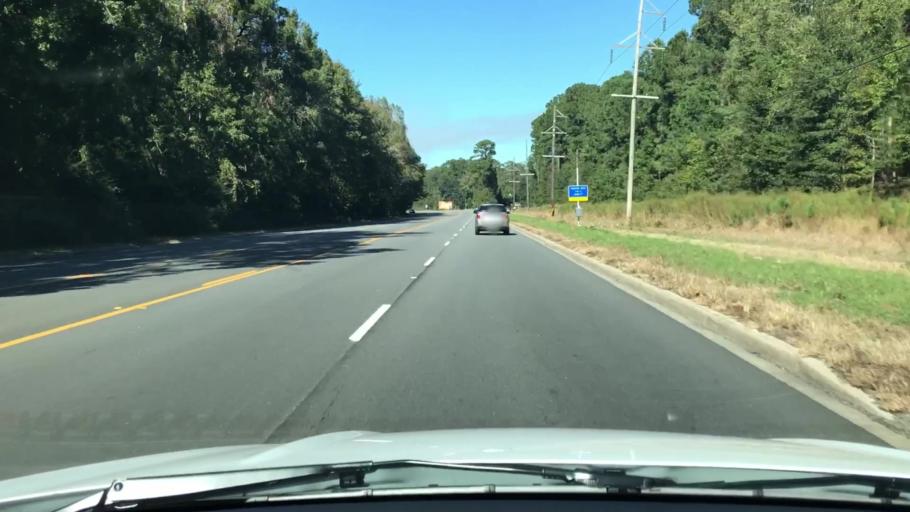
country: US
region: South Carolina
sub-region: Beaufort County
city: Laurel Bay
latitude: 32.5816
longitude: -80.7430
